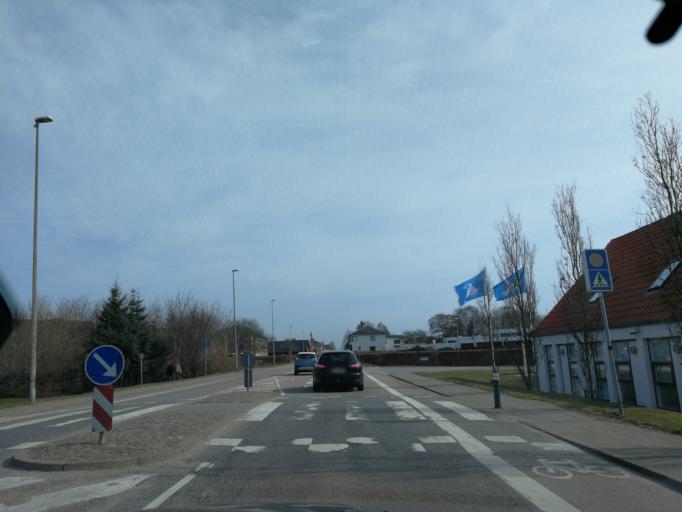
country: DK
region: North Denmark
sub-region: Alborg Kommune
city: Vodskov
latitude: 57.1029
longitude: 10.0250
